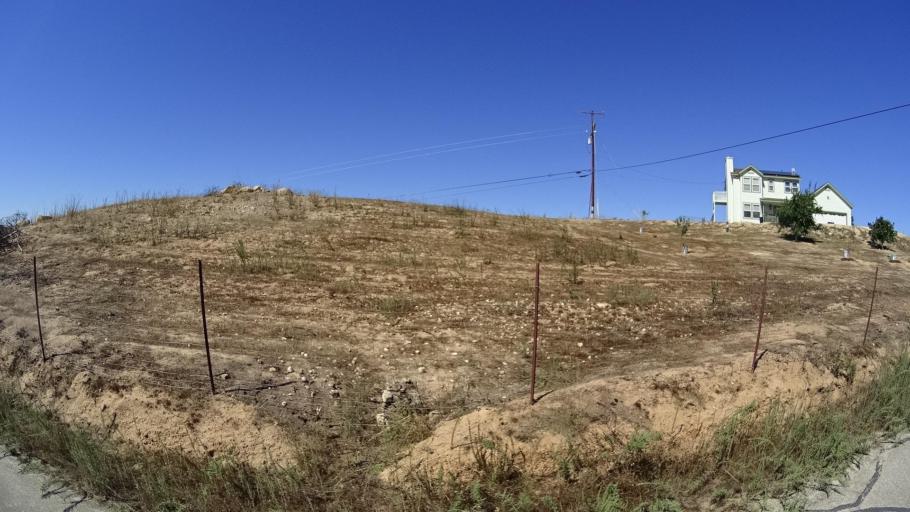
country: US
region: California
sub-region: San Diego County
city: Alpine
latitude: 32.7687
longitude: -116.7632
